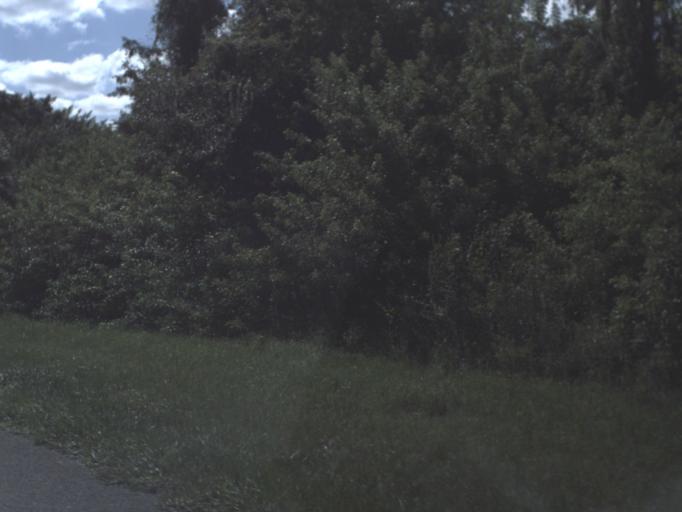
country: US
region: Florida
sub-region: Collier County
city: Lely Resort
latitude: 26.0279
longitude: -81.6439
